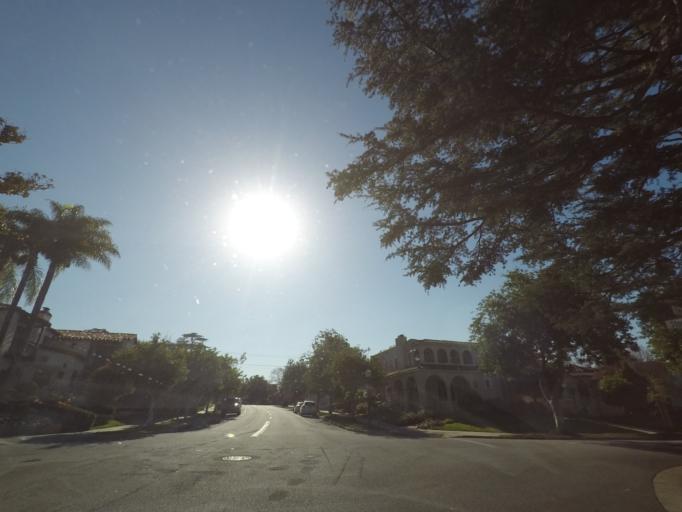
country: US
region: California
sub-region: Los Angeles County
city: North Glendale
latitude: 34.1629
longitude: -118.2454
